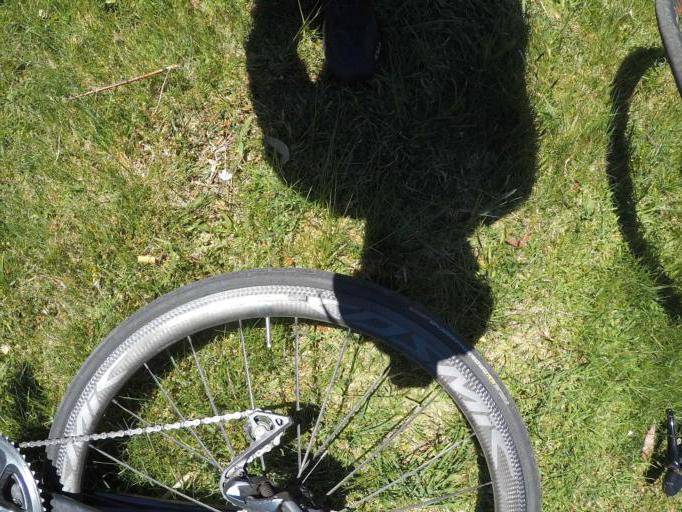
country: AU
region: New South Wales
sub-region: Lithgow
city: Bowenfels
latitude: -33.6393
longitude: 150.0582
